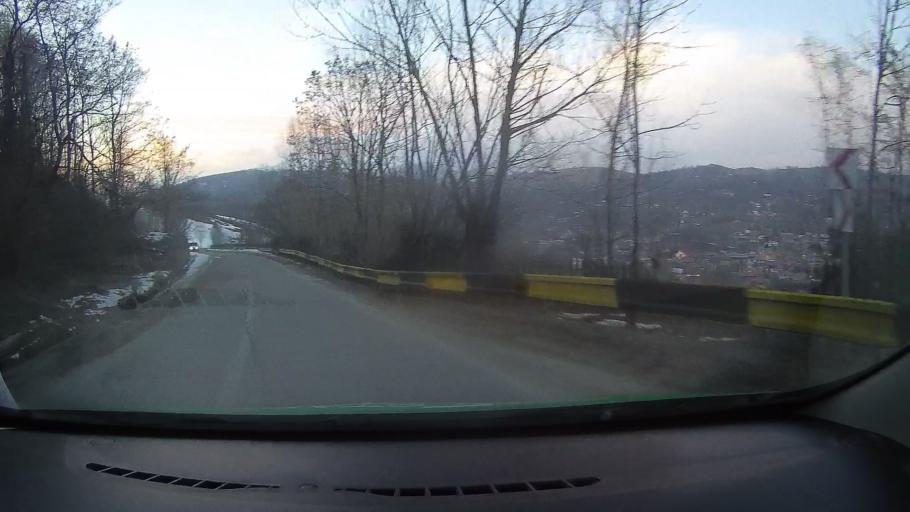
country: RO
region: Prahova
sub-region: Comuna Secaria
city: Secaria
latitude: 45.2706
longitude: 25.6834
